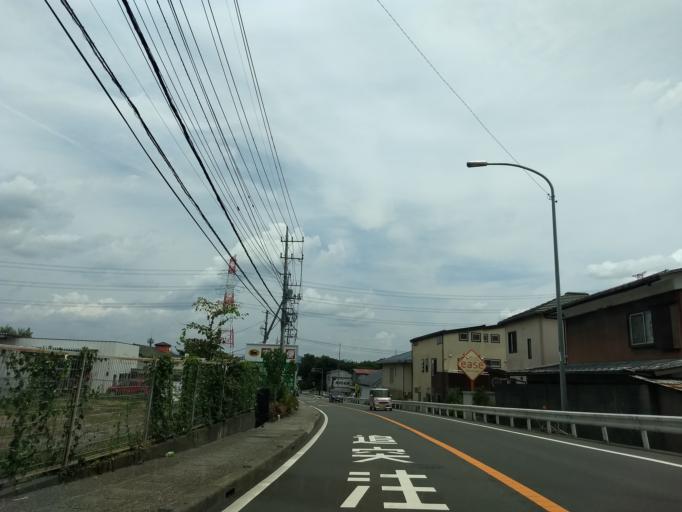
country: JP
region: Yamanashi
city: Otsuki
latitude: 35.5281
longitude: 138.8576
